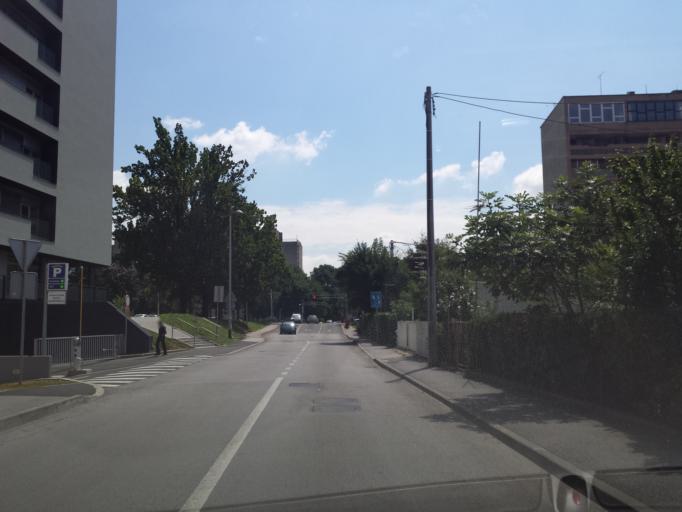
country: HR
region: Grad Zagreb
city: Zagreb - Centar
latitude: 45.8009
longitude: 15.9676
